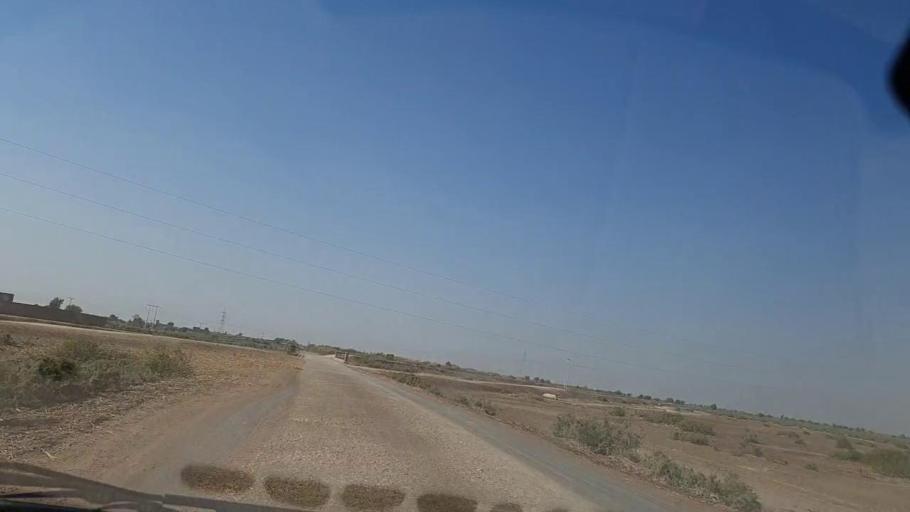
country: PK
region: Sindh
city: Mirpur Khas
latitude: 25.5196
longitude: 68.9484
